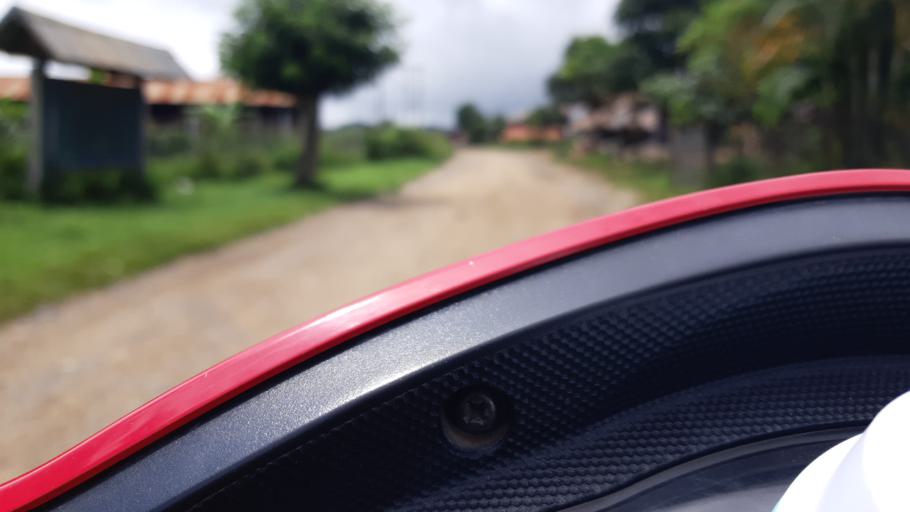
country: LA
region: Loungnamtha
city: Muang Nale
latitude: 20.0010
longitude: 101.5240
